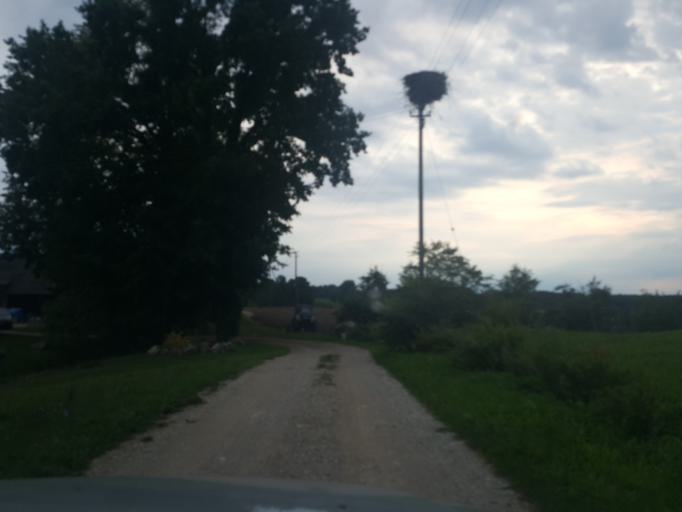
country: LT
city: Veisiejai
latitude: 54.1196
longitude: 23.5931
